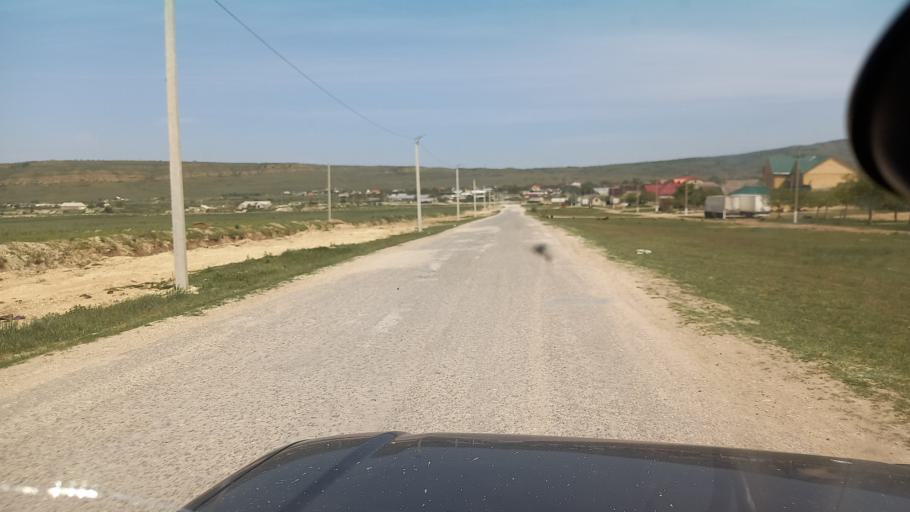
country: RU
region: Dagestan
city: Gurbuki
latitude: 42.6171
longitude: 47.5876
